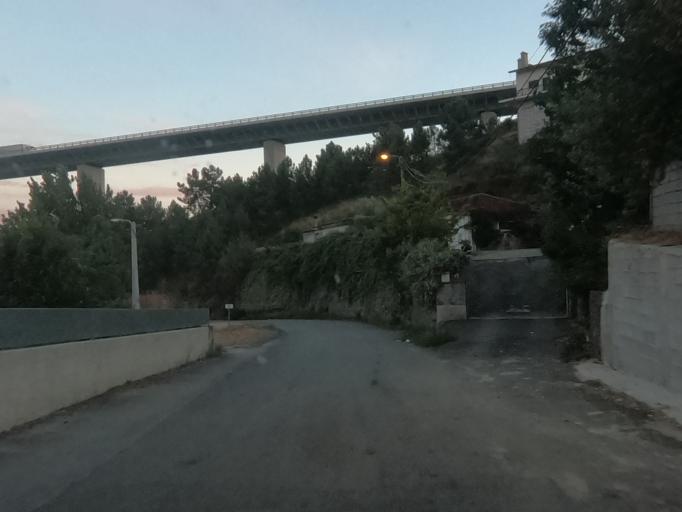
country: PT
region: Vila Real
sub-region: Vila Real
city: Vila Real
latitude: 41.2803
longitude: -7.7579
